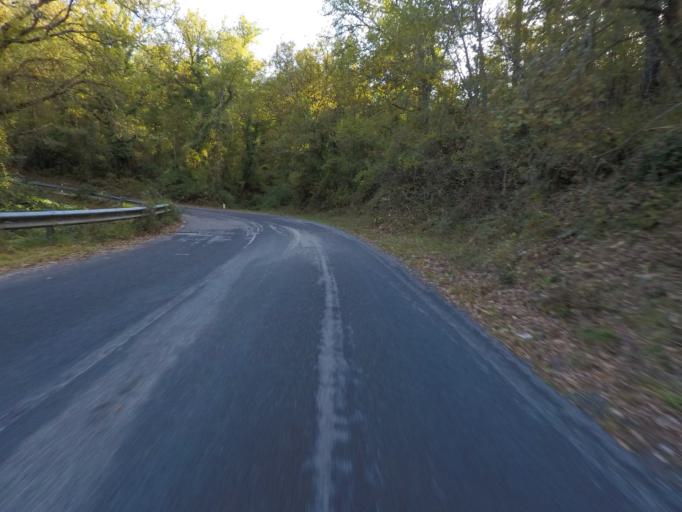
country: IT
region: Tuscany
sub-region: Provincia di Siena
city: Radda in Chianti
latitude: 43.4645
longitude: 11.3818
